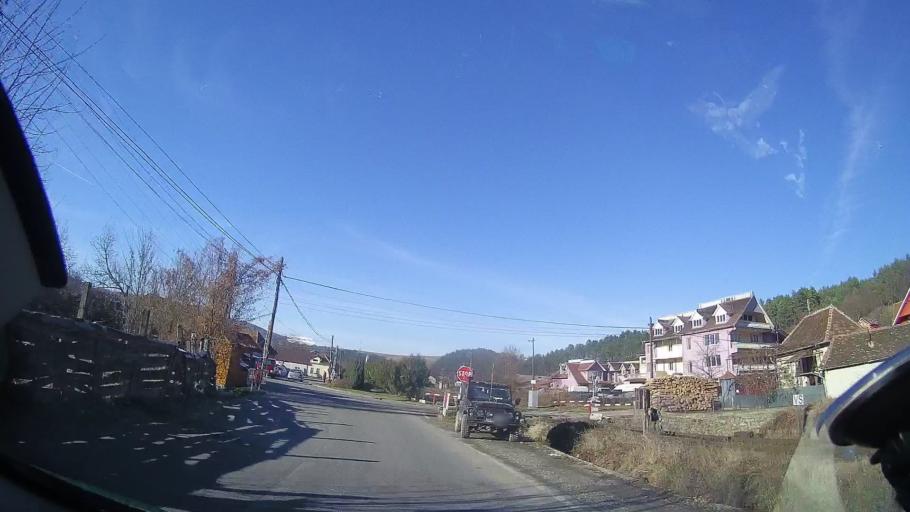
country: RO
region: Bihor
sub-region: Comuna Bratca
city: Bratca
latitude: 46.9276
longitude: 22.6068
